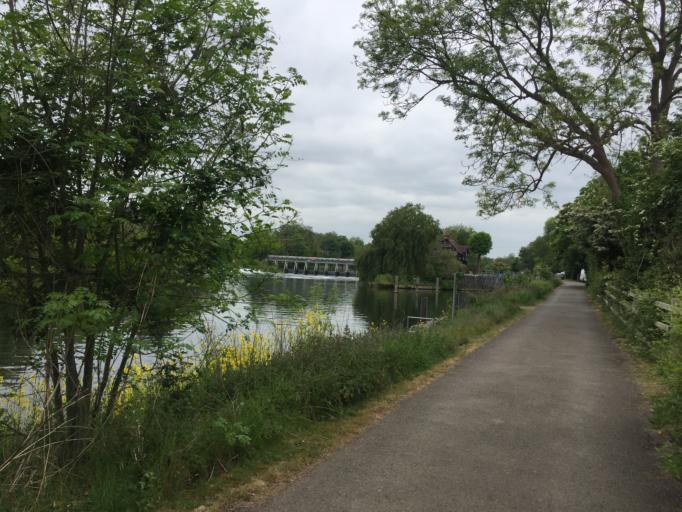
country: GB
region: England
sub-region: Royal Borough of Windsor and Maidenhead
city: Bray
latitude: 51.5088
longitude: -0.6883
